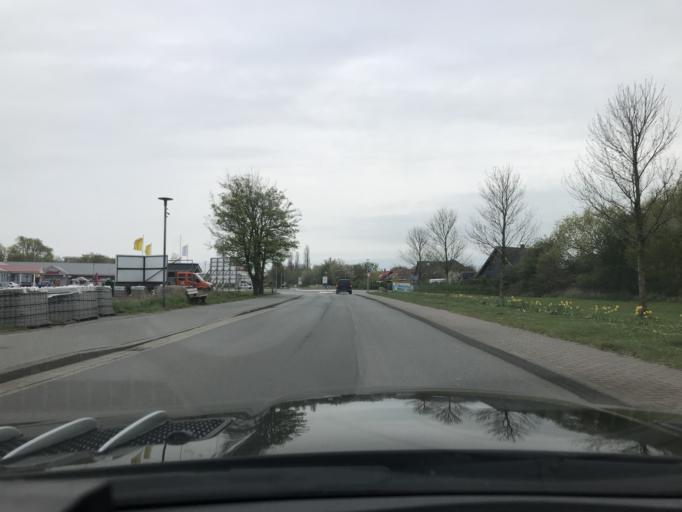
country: DE
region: Schleswig-Holstein
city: Grossenbrode
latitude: 54.3640
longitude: 11.0840
